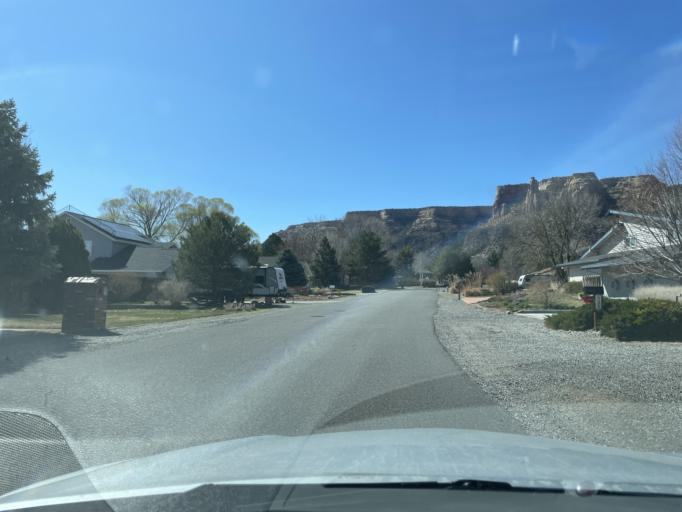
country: US
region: Colorado
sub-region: Mesa County
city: Redlands
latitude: 39.0828
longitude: -108.6718
